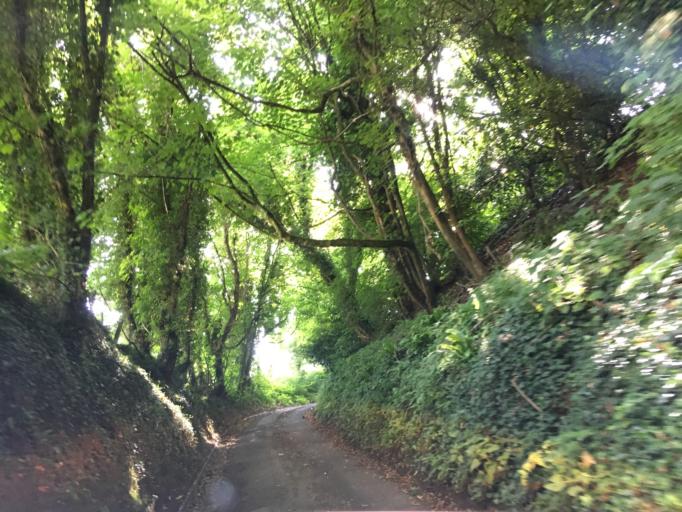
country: GB
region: England
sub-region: Gloucestershire
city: Brimscombe
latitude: 51.7162
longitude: -2.1805
